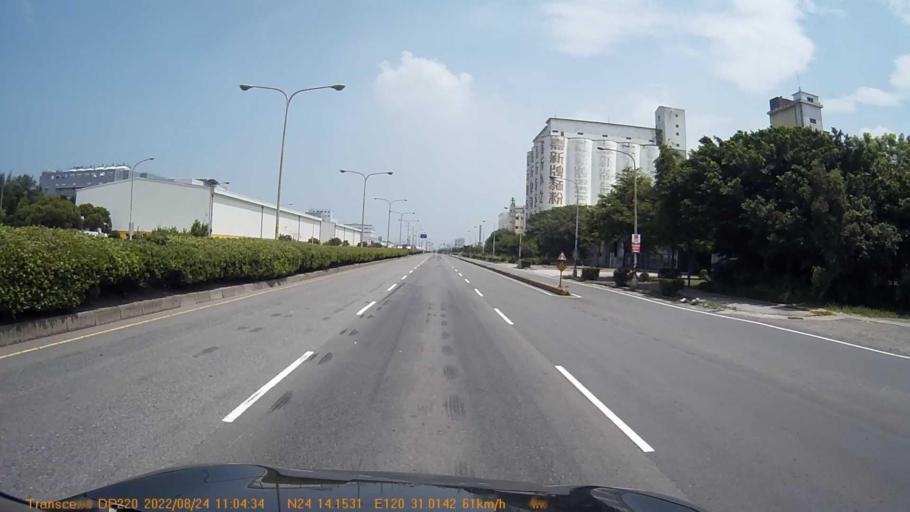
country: TW
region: Taiwan
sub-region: Changhua
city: Chang-hua
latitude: 24.2364
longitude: 120.5171
